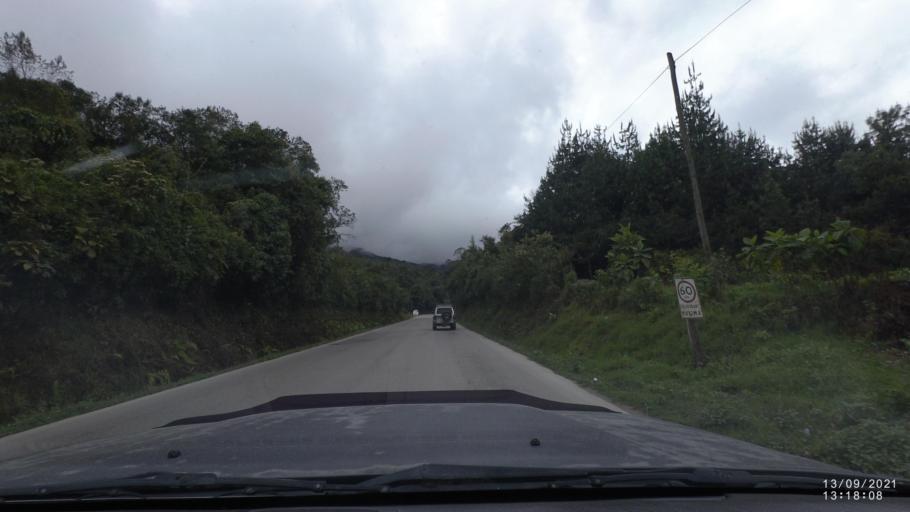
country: BO
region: Cochabamba
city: Colomi
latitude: -17.2008
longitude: -65.8639
